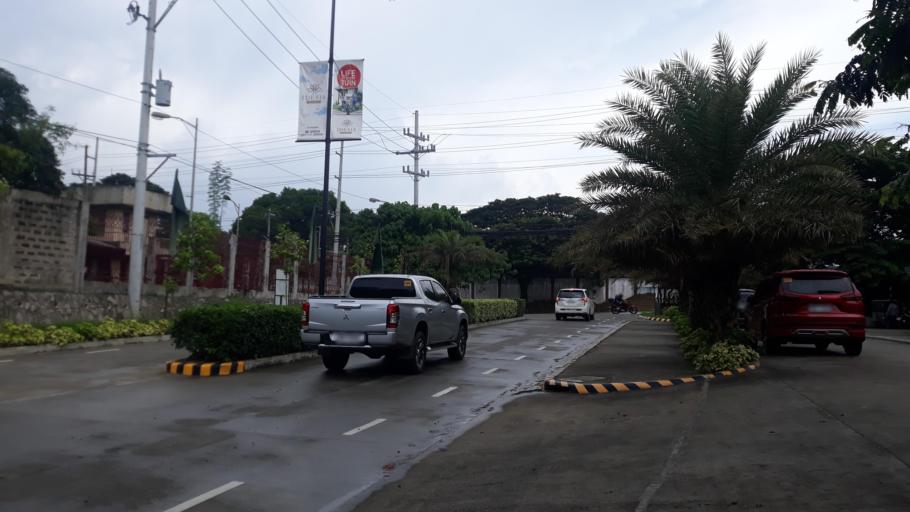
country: PH
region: Calabarzon
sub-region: Province of Cavite
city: Dasmarinas
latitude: 14.2997
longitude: 120.9499
